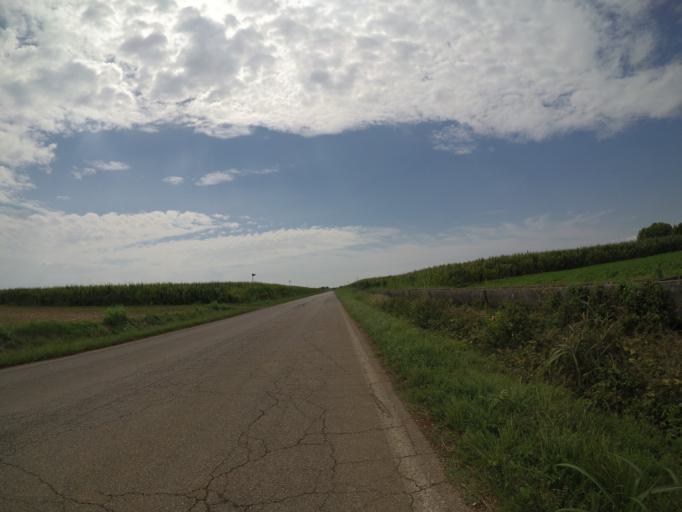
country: IT
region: Friuli Venezia Giulia
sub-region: Provincia di Udine
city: Bertiolo
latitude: 45.9664
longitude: 13.0900
